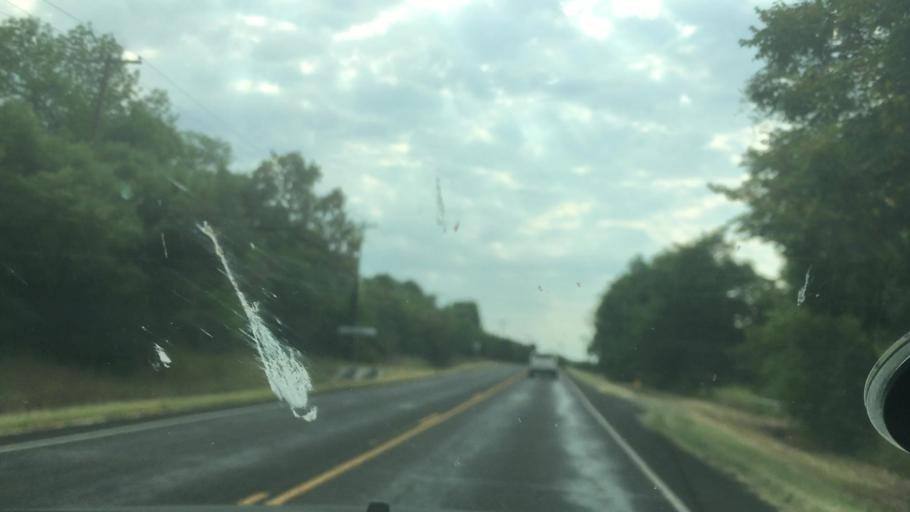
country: US
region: Texas
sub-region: Grayson County
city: Denison
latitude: 33.7838
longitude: -96.5923
